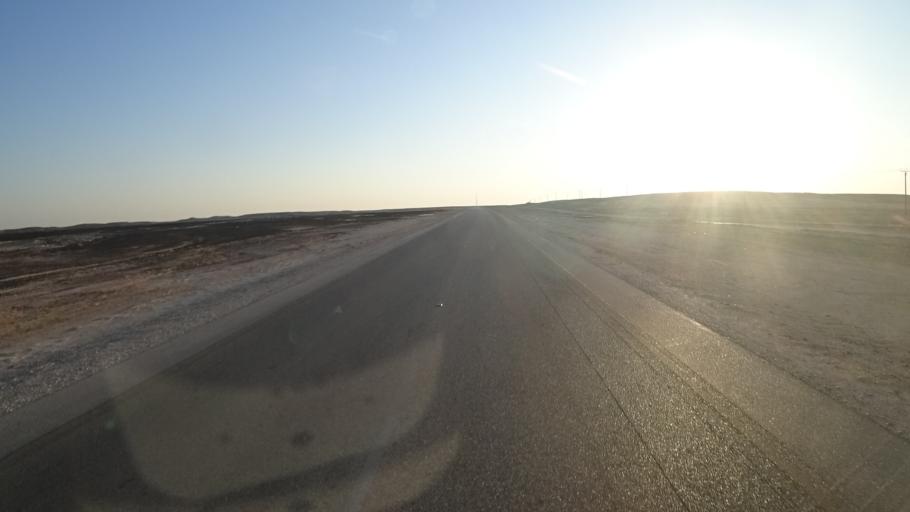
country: OM
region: Zufar
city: Salalah
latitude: 17.5502
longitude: 53.4278
